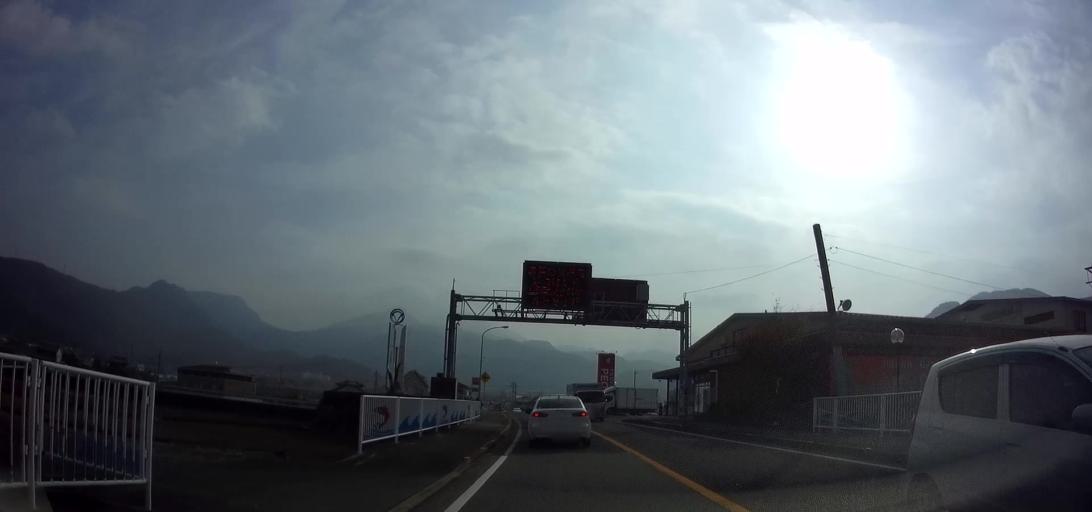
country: JP
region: Nagasaki
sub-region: Isahaya-shi
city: Isahaya
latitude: 32.7887
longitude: 130.1900
